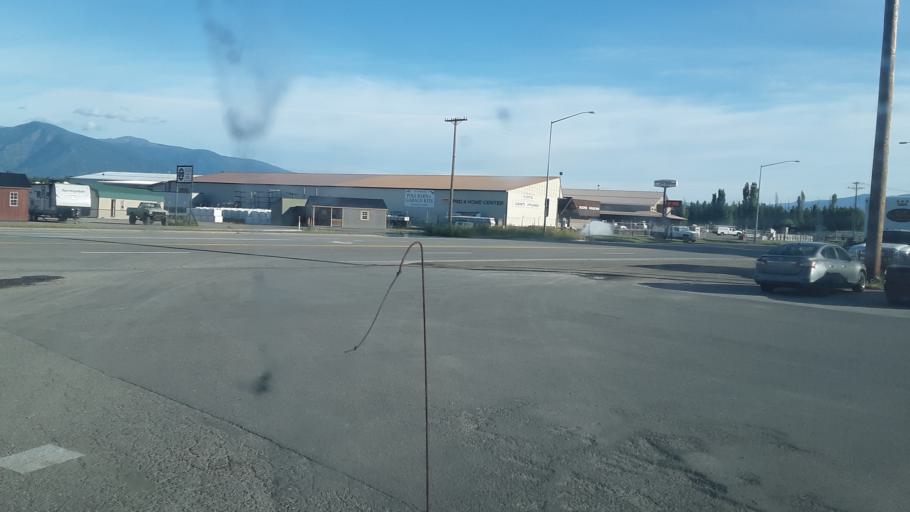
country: US
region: Idaho
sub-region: Boundary County
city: Bonners Ferry
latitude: 48.7315
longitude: -116.2988
